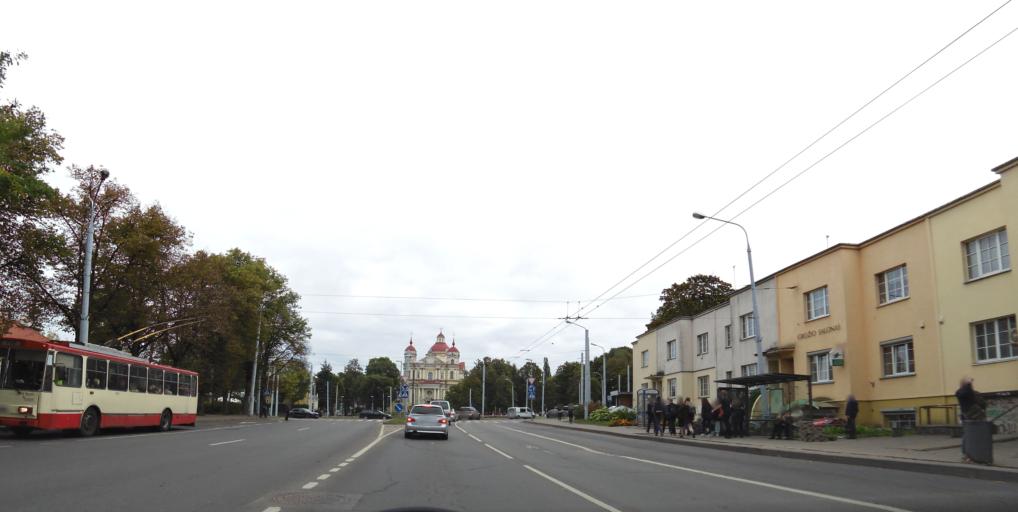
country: LT
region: Vilnius County
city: Rasos
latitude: 54.6928
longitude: 25.3029
